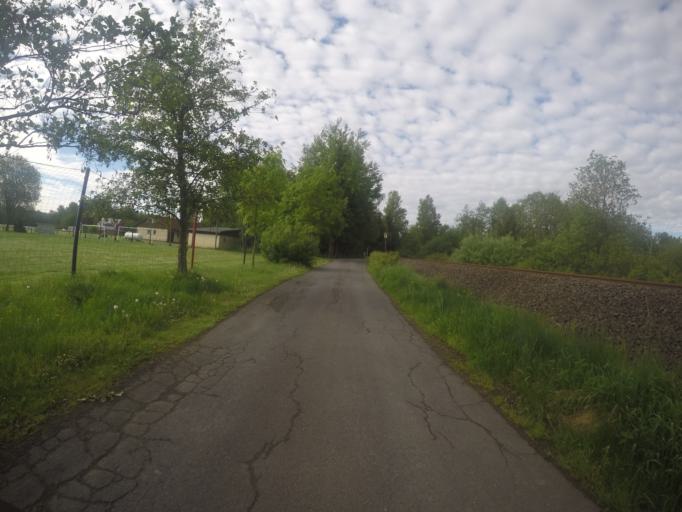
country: DE
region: Bavaria
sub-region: Upper Franconia
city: Schonwald
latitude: 50.2099
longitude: 12.1016
